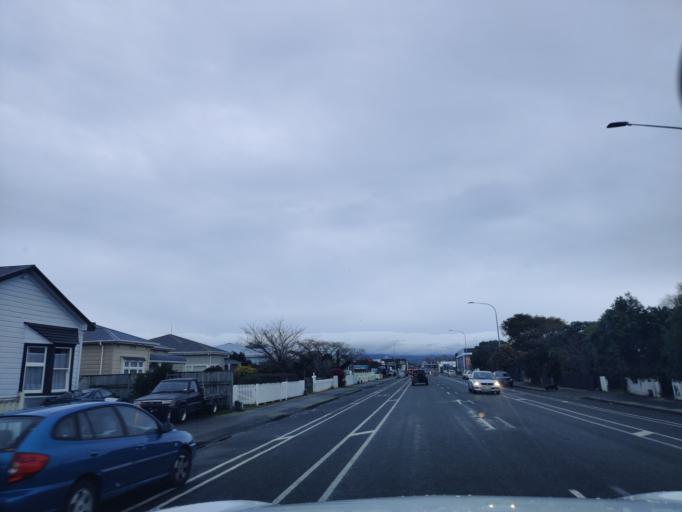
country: NZ
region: Manawatu-Wanganui
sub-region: Palmerston North City
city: Palmerston North
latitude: -40.3535
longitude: 175.6028
